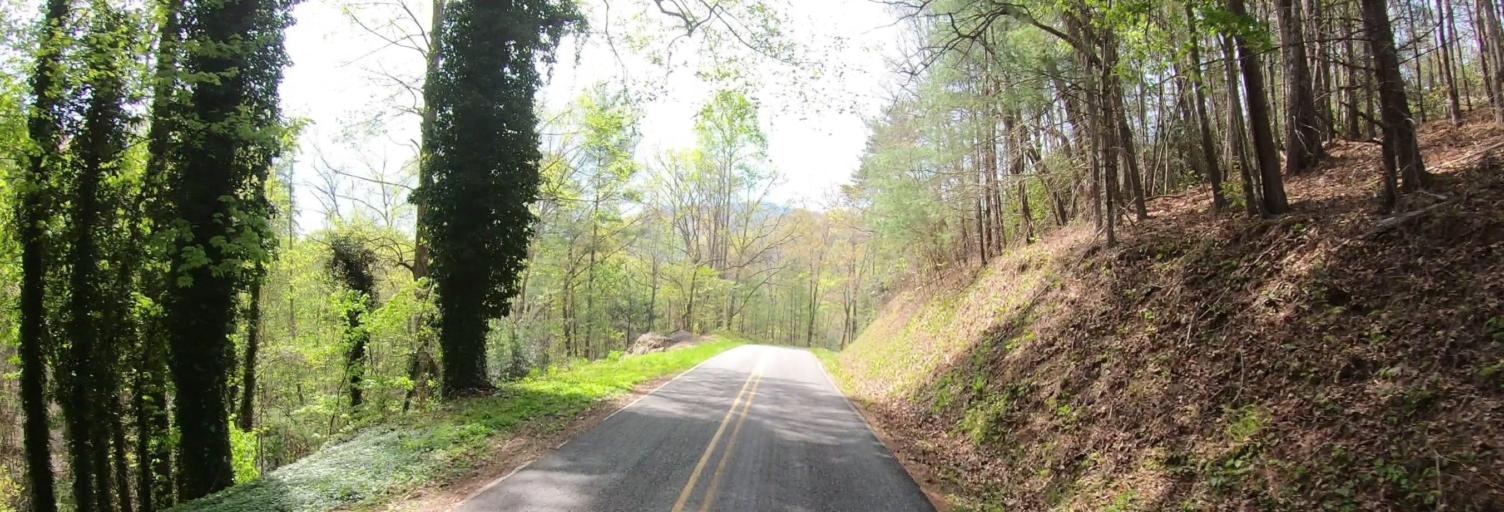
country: US
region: North Carolina
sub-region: Graham County
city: Robbinsville
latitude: 35.3800
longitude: -83.8734
